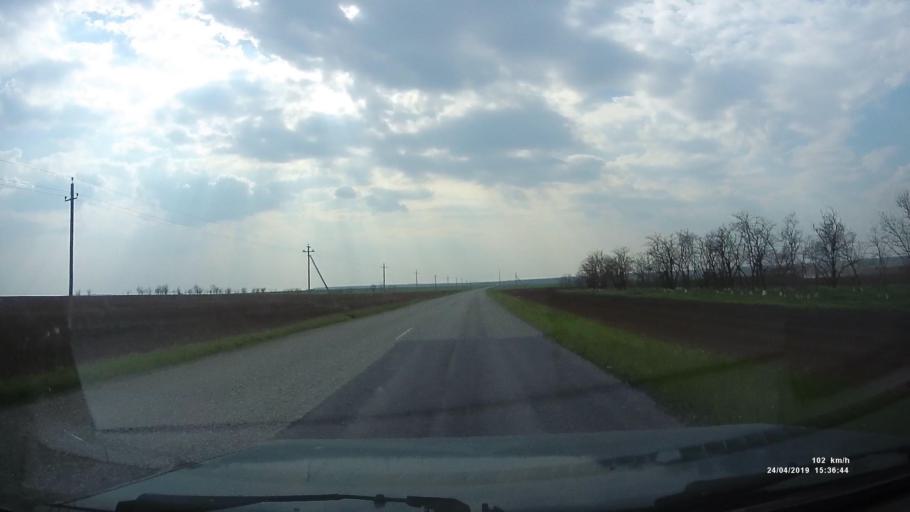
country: RU
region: Kalmykiya
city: Yashalta
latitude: 46.5988
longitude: 42.8653
